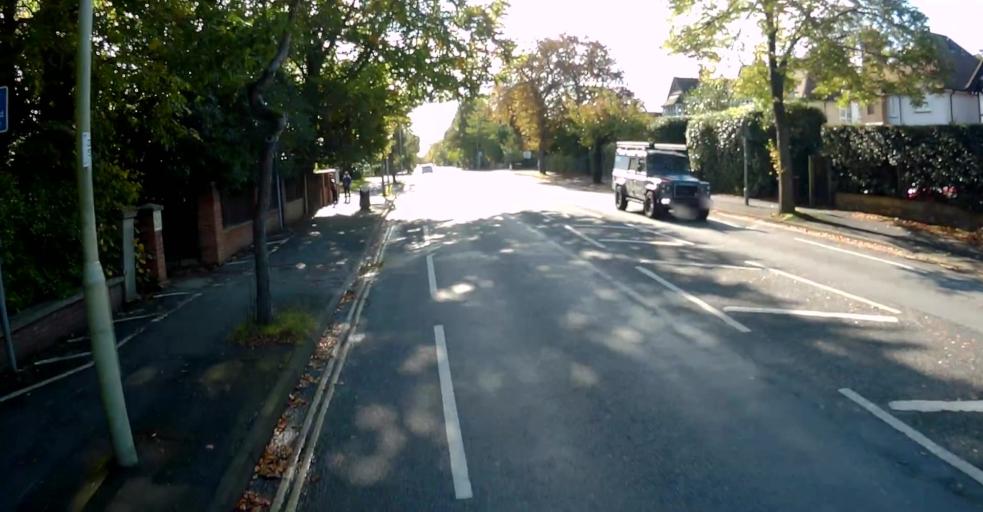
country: GB
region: England
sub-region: Hampshire
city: Farnborough
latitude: 51.2846
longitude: -0.7509
